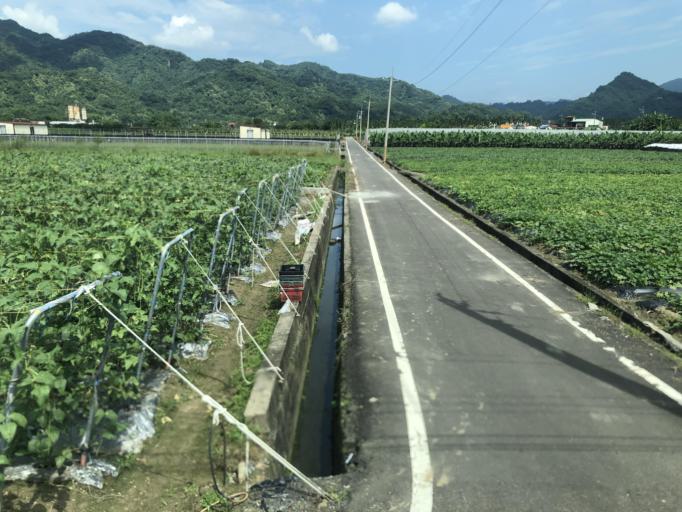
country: TW
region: Taiwan
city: Yujing
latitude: 22.9127
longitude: 120.5731
